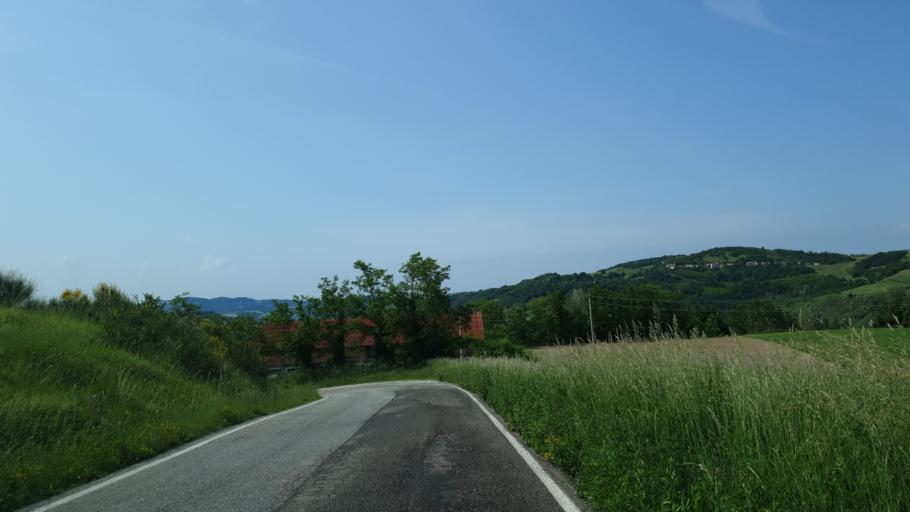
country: IT
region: Emilia-Romagna
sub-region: Provincia di Rimini
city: Sant'Agata Feltria
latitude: 43.9061
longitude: 12.2247
